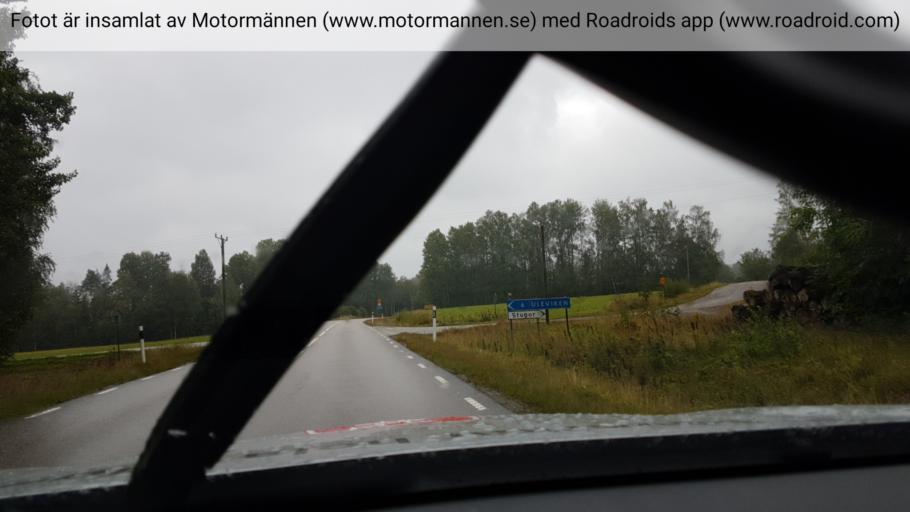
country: SE
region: Vaestra Goetaland
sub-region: Bengtsfors Kommun
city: Dals Langed
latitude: 58.8667
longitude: 12.1910
